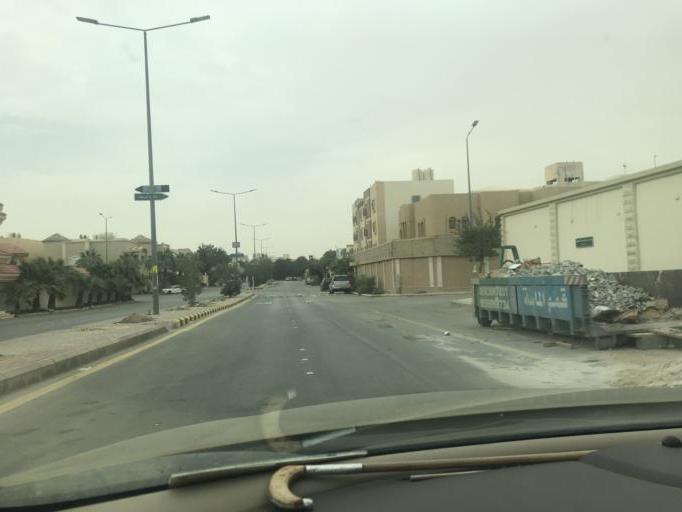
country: SA
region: Ar Riyad
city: Riyadh
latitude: 24.7371
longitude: 46.7565
